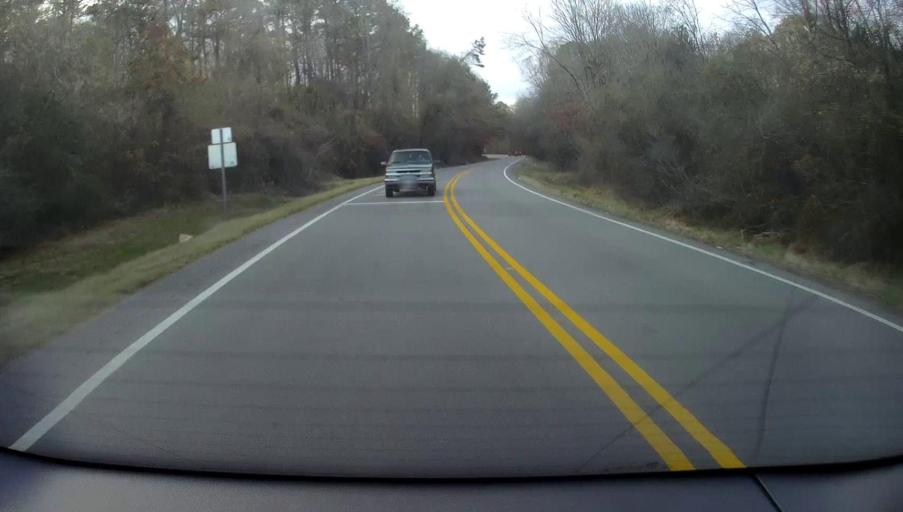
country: US
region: Alabama
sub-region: Etowah County
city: Attalla
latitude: 34.0373
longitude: -86.1129
